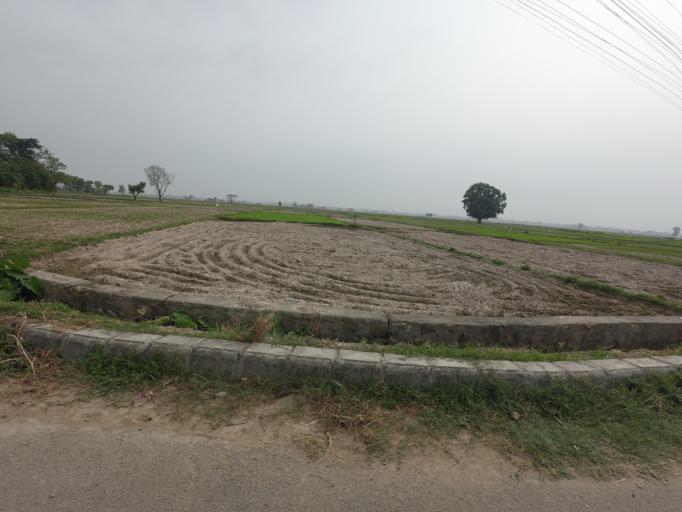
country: NP
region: Western Region
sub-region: Lumbini Zone
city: Bhairahawa
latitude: 27.4892
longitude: 83.4317
